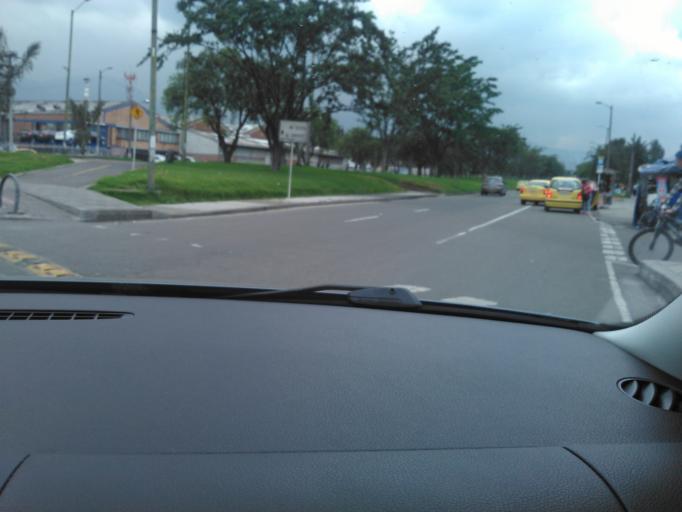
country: CO
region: Bogota D.C.
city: Bogota
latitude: 4.6263
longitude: -74.1072
